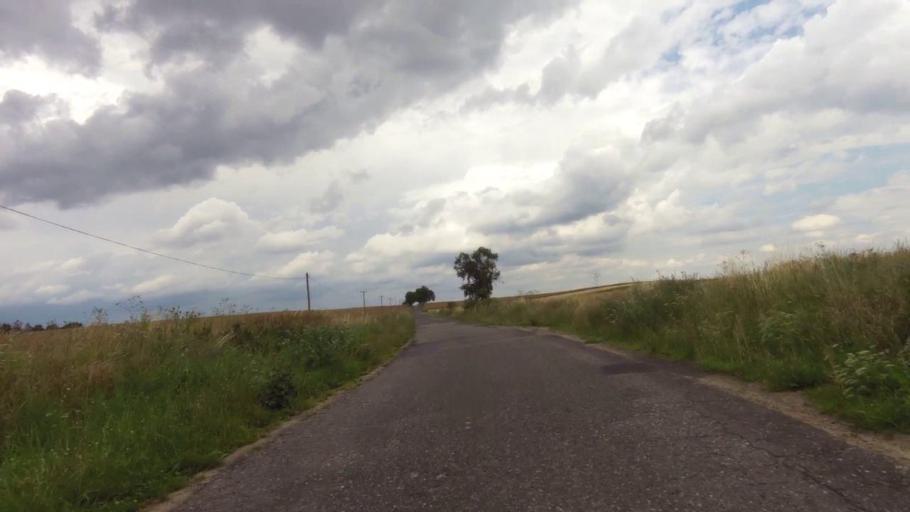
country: PL
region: West Pomeranian Voivodeship
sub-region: Powiat gryfinski
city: Moryn
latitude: 52.8777
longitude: 14.3933
